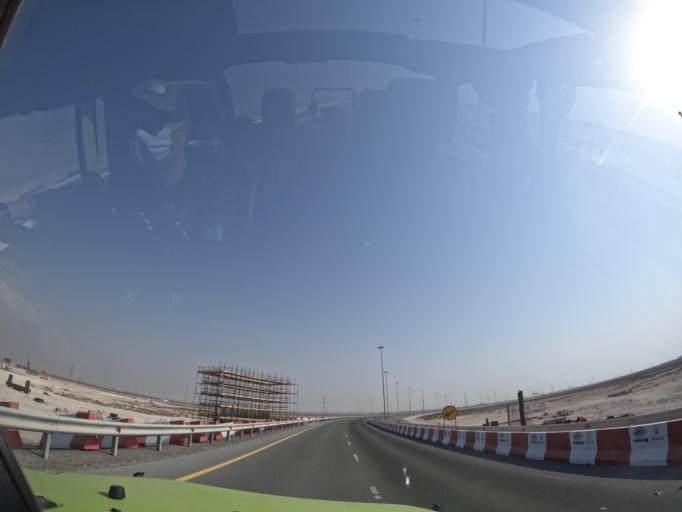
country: AE
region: Abu Dhabi
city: Abu Dhabi
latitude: 24.6770
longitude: 54.8116
